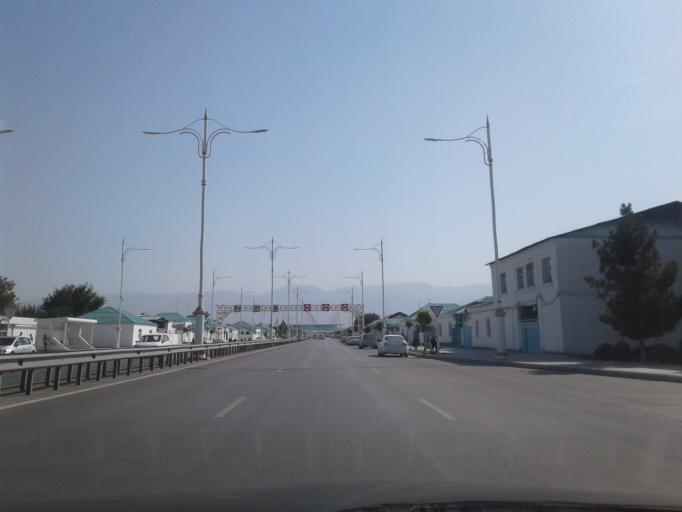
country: TM
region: Ahal
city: Ashgabat
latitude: 37.9567
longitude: 58.4153
